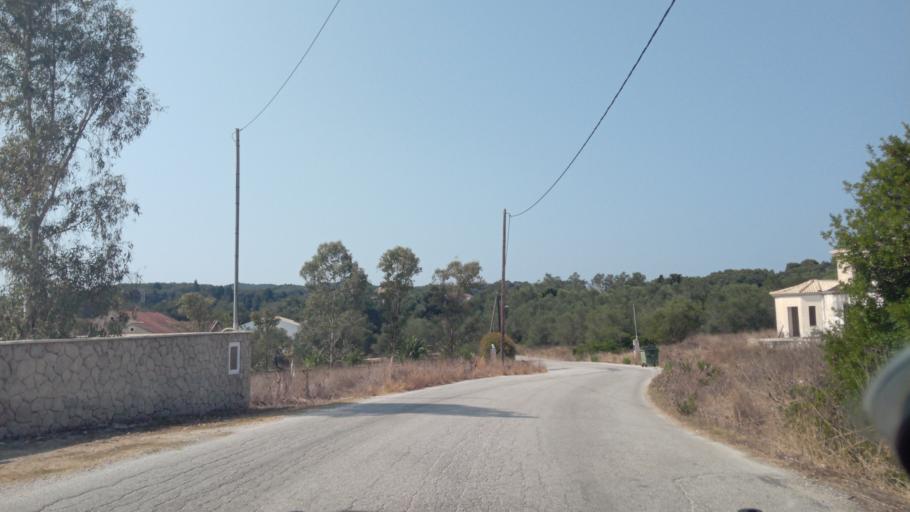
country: GR
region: Ionian Islands
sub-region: Nomos Kerkyras
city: Perivoli
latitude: 39.4139
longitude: 20.0293
